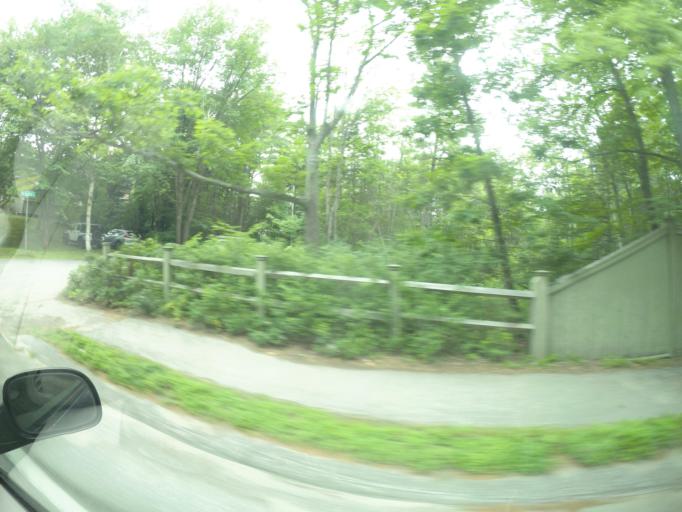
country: US
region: Maine
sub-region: York County
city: Kennebunkport
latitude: 43.3546
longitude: -70.4792
